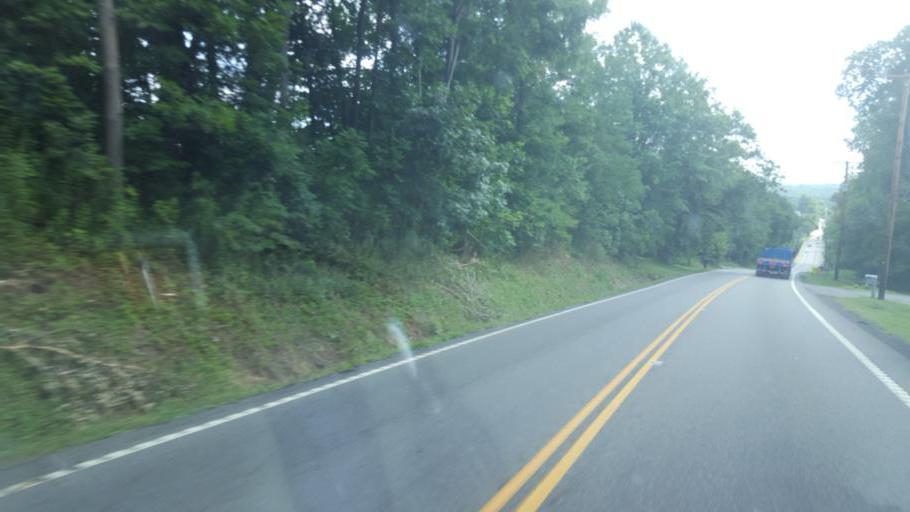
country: US
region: Ohio
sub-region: Columbiana County
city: Lisbon
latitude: 40.7721
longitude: -80.7837
